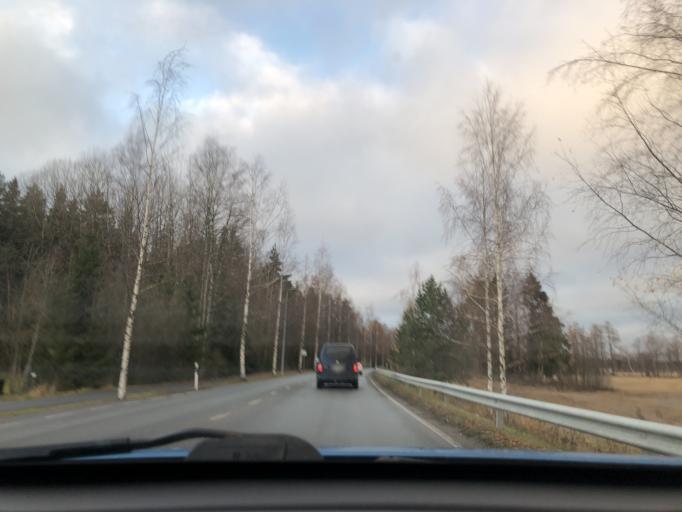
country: FI
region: Pirkanmaa
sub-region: Tampere
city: Kangasala
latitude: 61.4678
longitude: 24.0633
